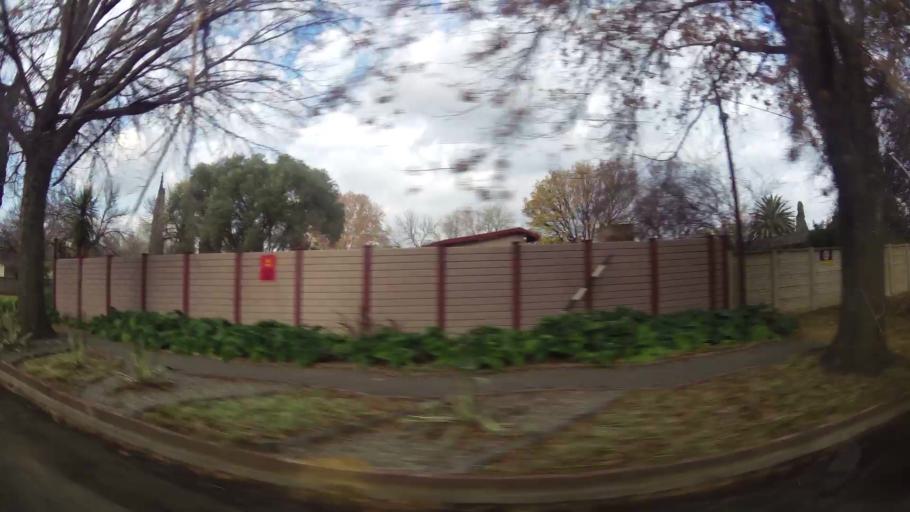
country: ZA
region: Orange Free State
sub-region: Fezile Dabi District Municipality
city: Sasolburg
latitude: -26.8010
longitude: 27.8186
